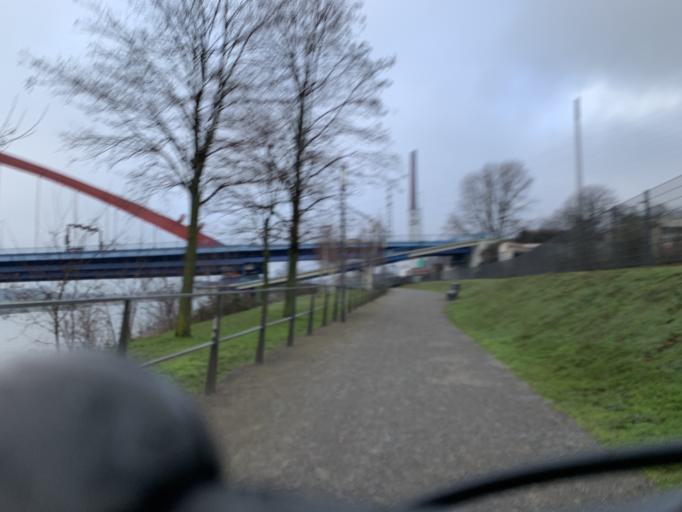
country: DE
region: North Rhine-Westphalia
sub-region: Regierungsbezirk Dusseldorf
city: Hochfeld
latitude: 51.4153
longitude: 6.7415
